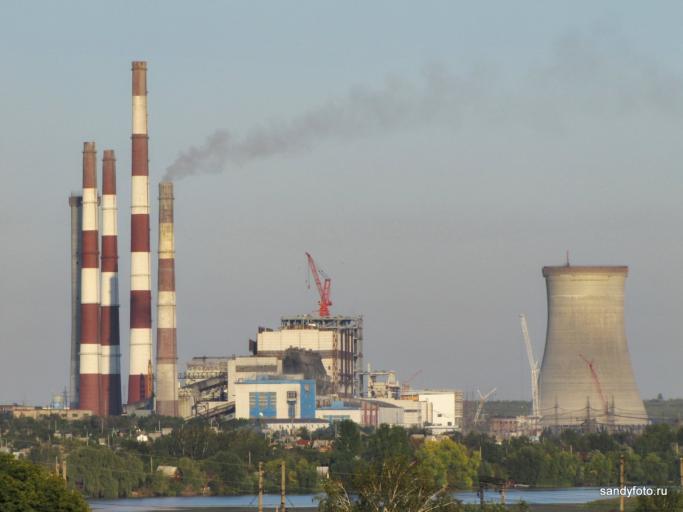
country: RU
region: Chelyabinsk
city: Troitsk
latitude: 54.0488
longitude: 61.5970
